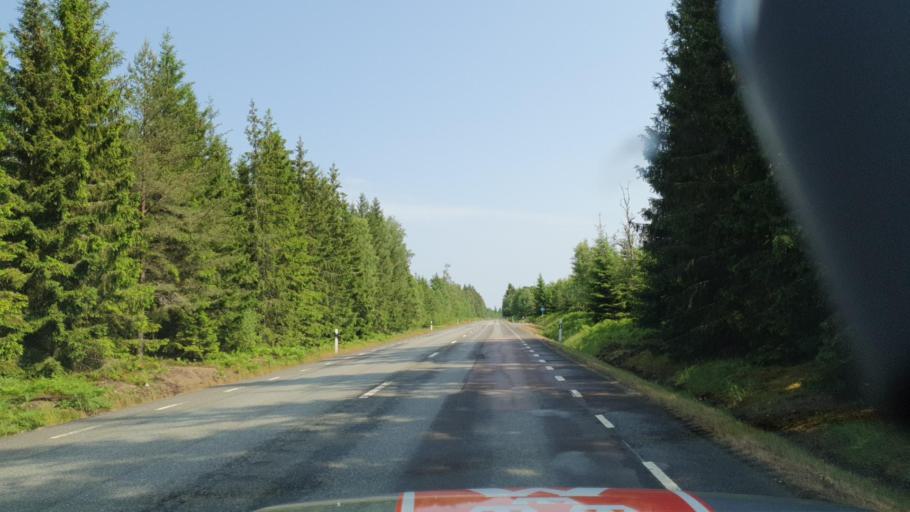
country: SE
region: Kronoberg
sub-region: Uppvidinge Kommun
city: Lenhovda
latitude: 57.0375
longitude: 15.2142
